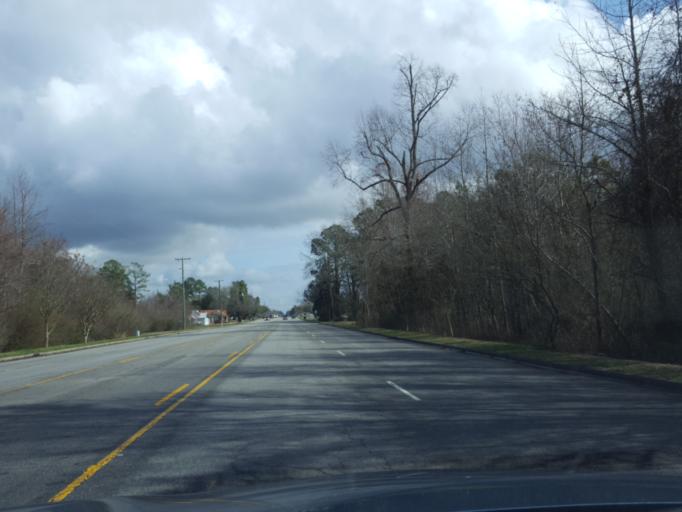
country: US
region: North Carolina
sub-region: Washington County
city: Plymouth
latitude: 35.8700
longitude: -76.7047
